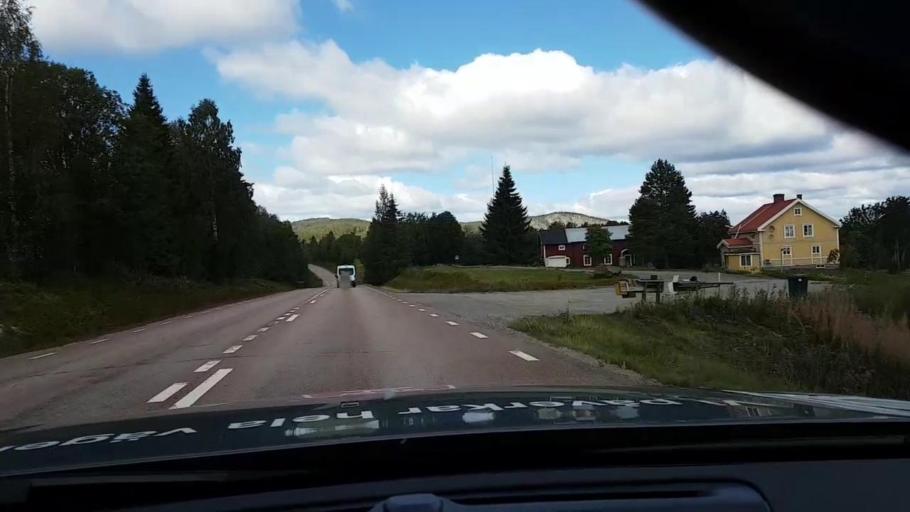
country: SE
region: Vaesternorrland
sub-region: OErnskoeldsviks Kommun
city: Bjasta
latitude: 63.3708
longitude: 18.4386
